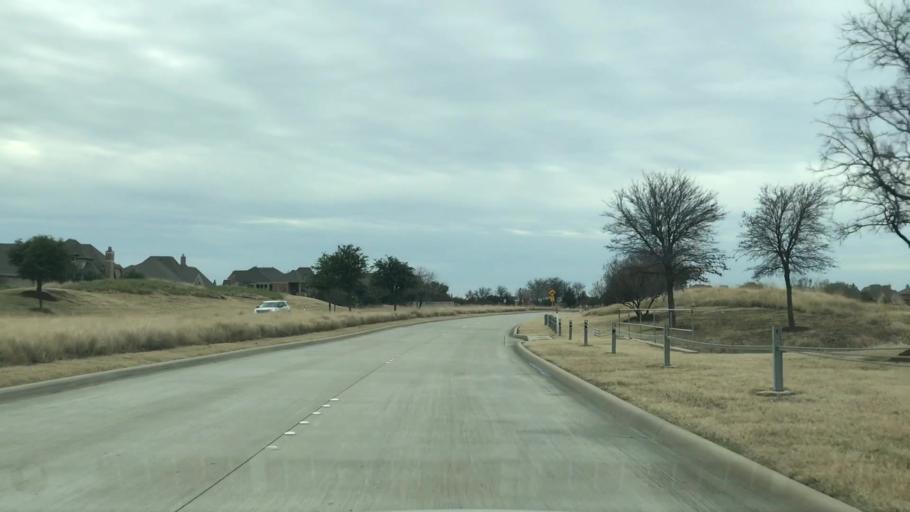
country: US
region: Texas
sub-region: Denton County
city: The Colony
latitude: 33.1162
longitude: -96.9151
